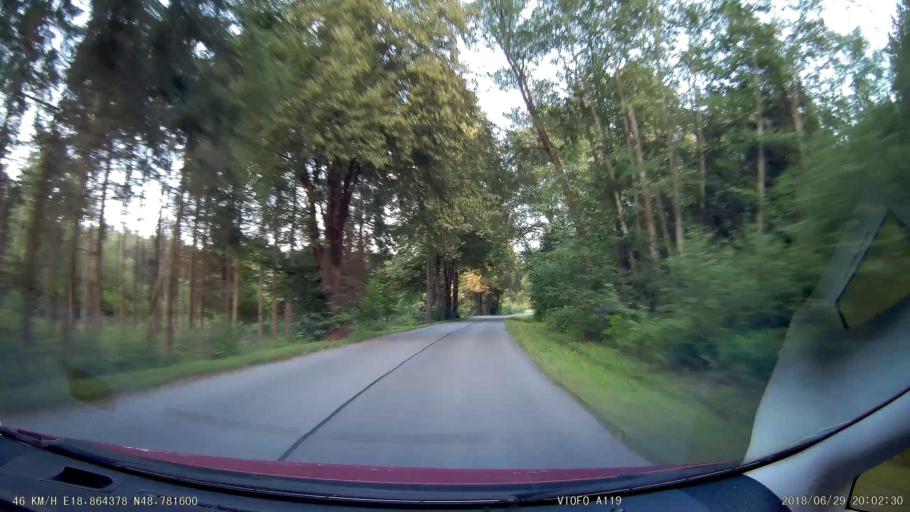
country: SK
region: Banskobystricky
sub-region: Okres Ziar nad Hronom
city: Kremnica
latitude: 48.7818
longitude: 18.8644
